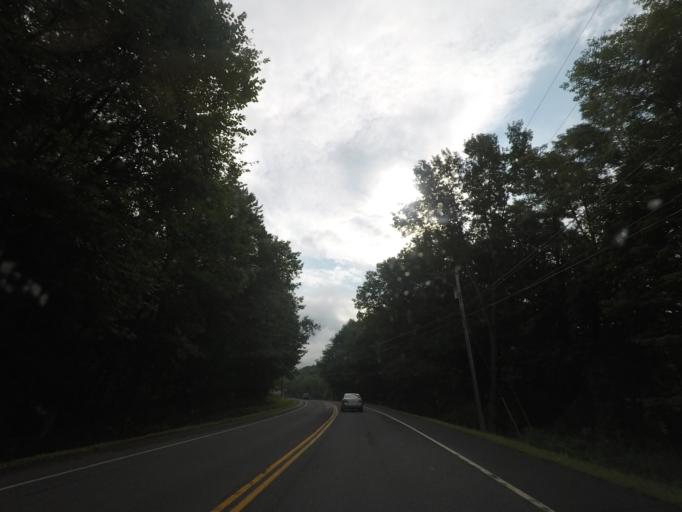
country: US
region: New York
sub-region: Rensselaer County
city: Nassau
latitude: 42.4946
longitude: -73.5495
